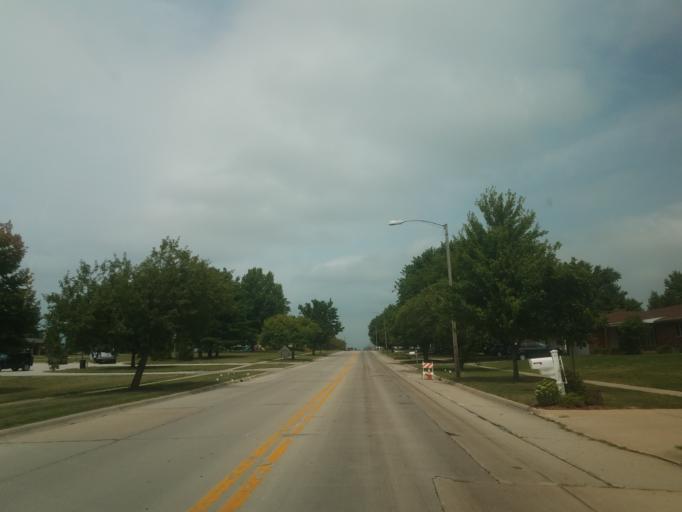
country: US
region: Illinois
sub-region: McLean County
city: Normal
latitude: 40.5142
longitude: -89.0211
